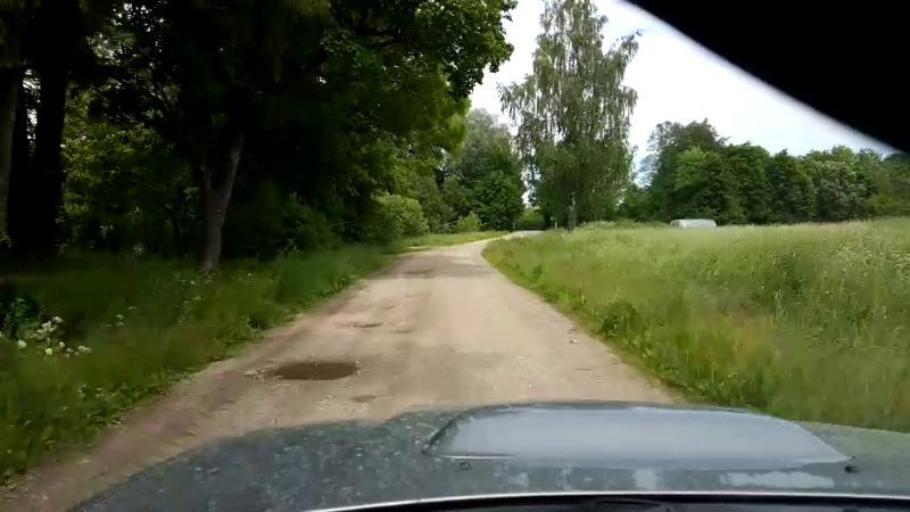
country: EE
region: Paernumaa
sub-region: Tootsi vald
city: Tootsi
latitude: 58.5378
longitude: 24.7338
